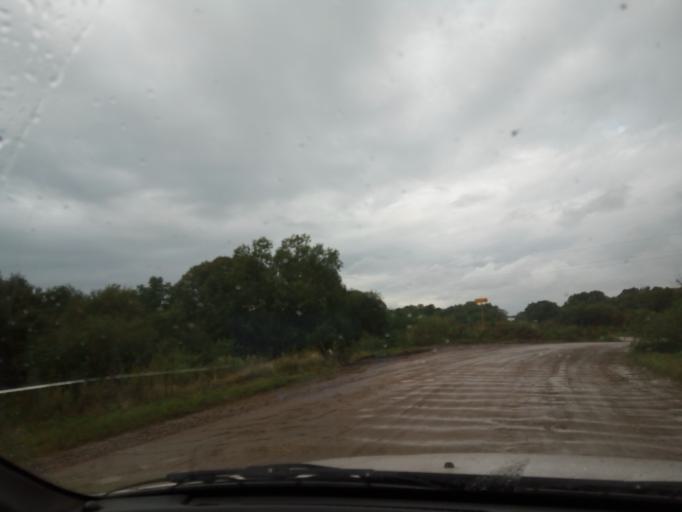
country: RU
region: Primorskiy
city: Lazo
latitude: 45.8524
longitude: 133.6461
